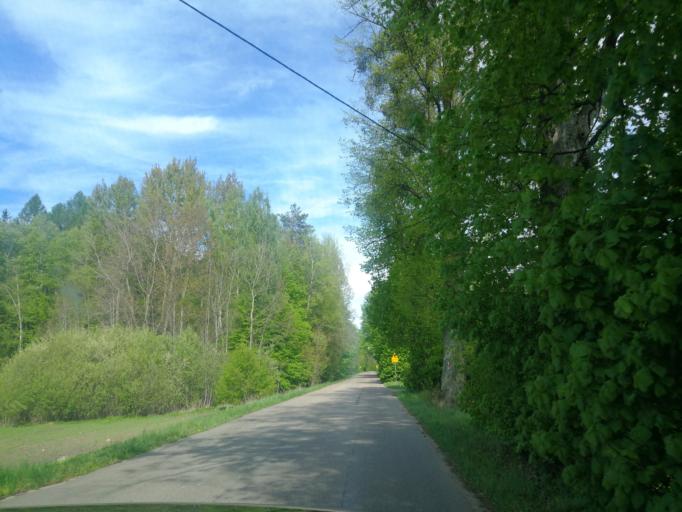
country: PL
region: Warmian-Masurian Voivodeship
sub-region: Powiat ilawski
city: Ilawa
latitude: 53.6864
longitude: 19.6826
